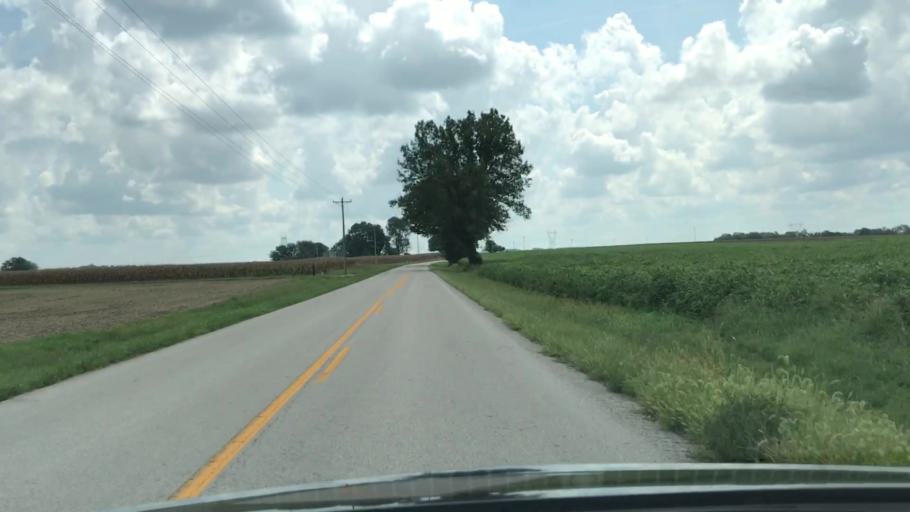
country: US
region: Kentucky
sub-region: Todd County
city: Elkton
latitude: 36.7819
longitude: -87.1240
